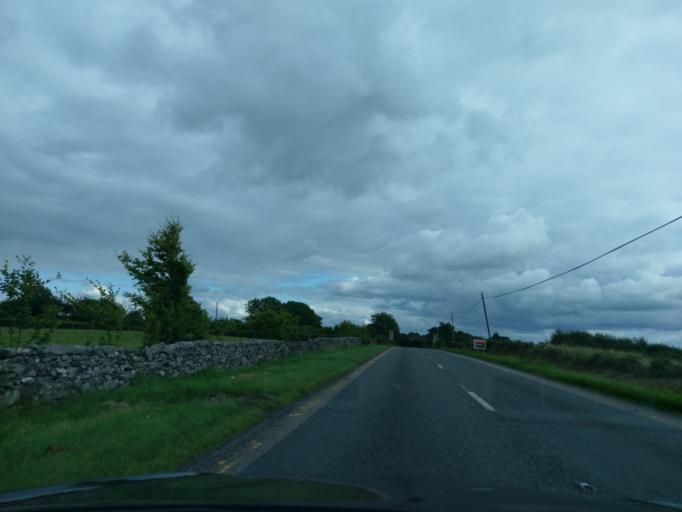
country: IE
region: Connaught
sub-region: County Galway
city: Oranmore
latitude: 53.1901
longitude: -8.8514
